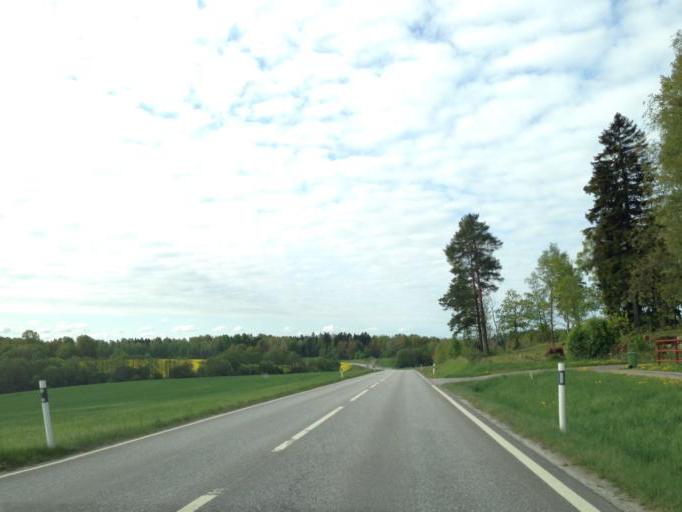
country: SE
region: Soedermanland
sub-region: Flens Kommun
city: Malmkoping
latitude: 59.0855
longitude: 16.8088
